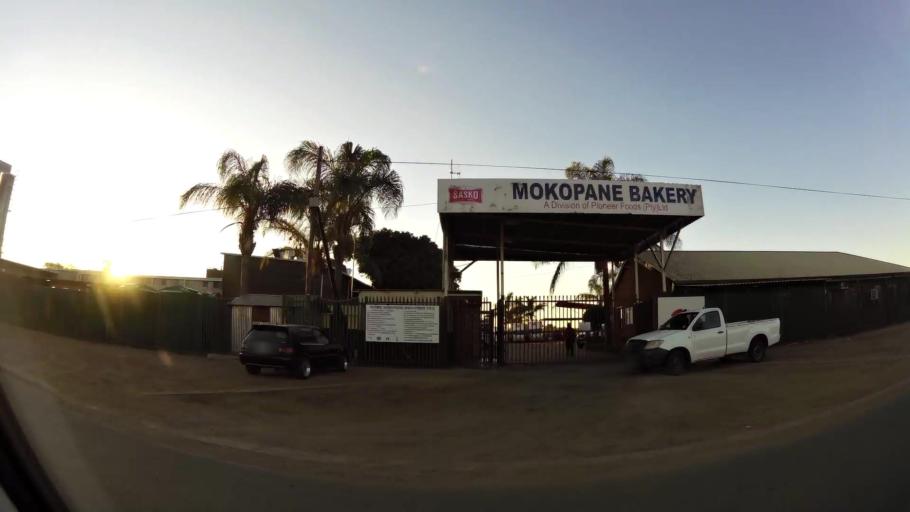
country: ZA
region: Limpopo
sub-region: Waterberg District Municipality
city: Mokopane
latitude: -24.1419
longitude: 28.9763
